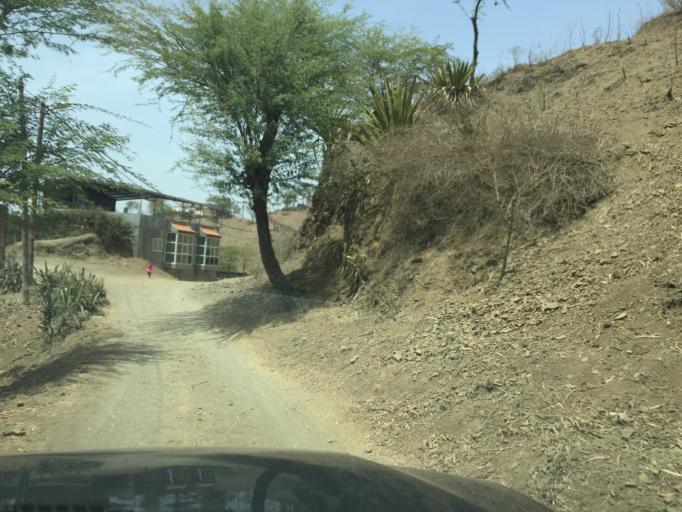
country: CV
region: Sao Salvador do Mundo
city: Picos
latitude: 15.1128
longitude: -23.6385
